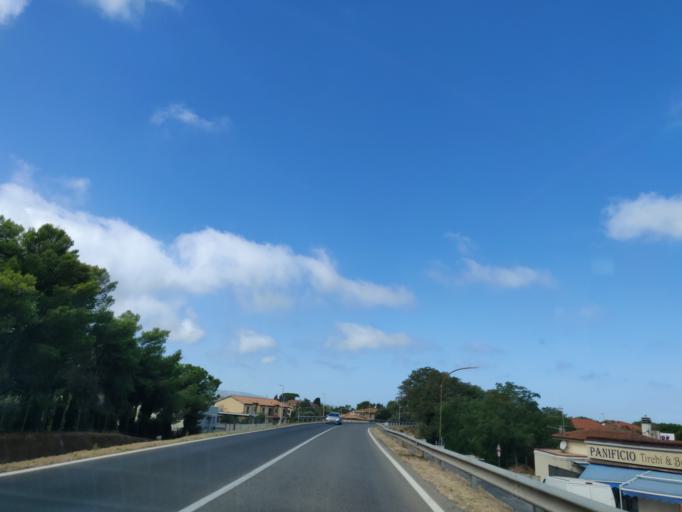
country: IT
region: Tuscany
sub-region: Provincia di Grosseto
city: Orbetello Scalo
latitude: 42.4467
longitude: 11.2479
